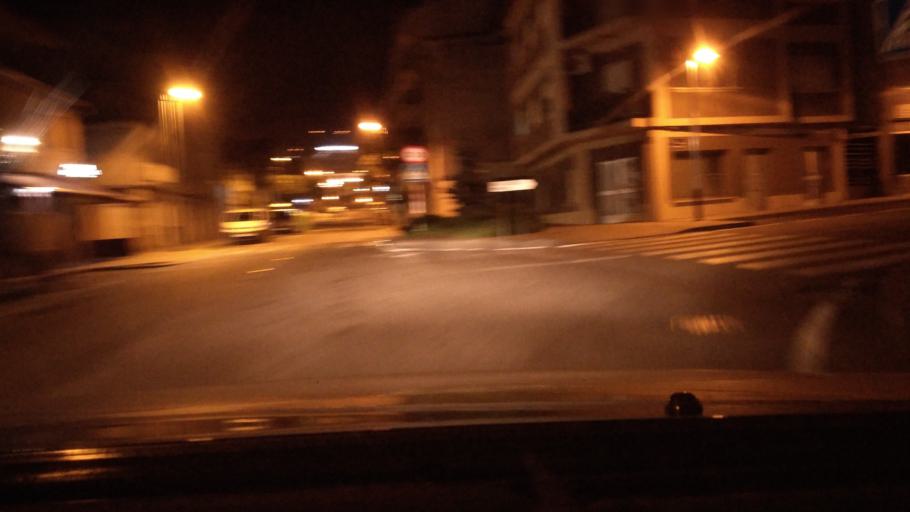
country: ES
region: Galicia
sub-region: Provincia de Pontevedra
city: Moana
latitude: 42.2874
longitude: -8.7342
